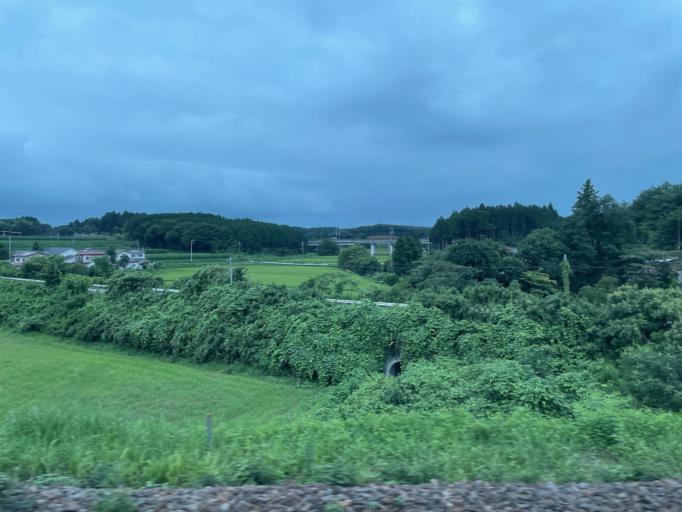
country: JP
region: Tochigi
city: Kuroiso
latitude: 36.9952
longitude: 140.0868
